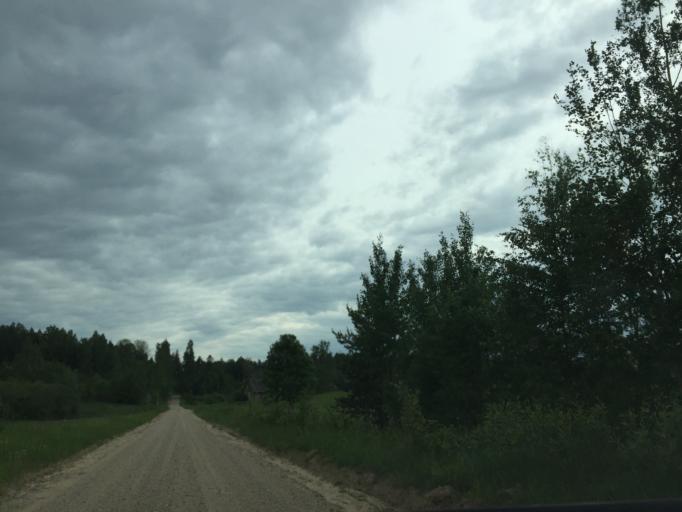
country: LV
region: Aglona
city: Aglona
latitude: 56.1543
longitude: 27.2262
